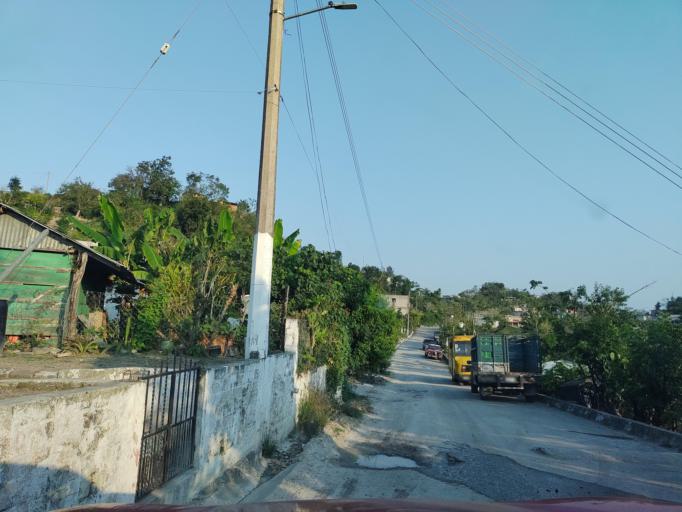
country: MX
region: Veracruz
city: Agua Dulce
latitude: 20.4057
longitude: -97.2914
